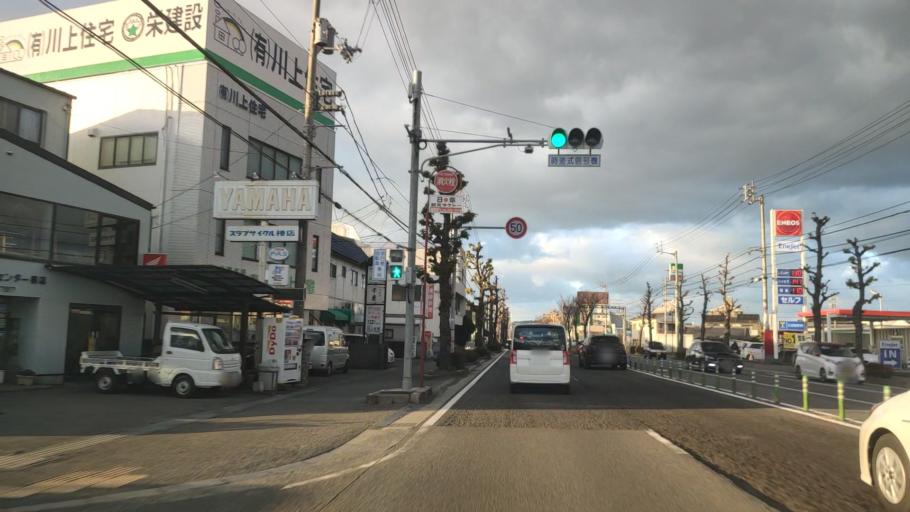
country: JP
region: Ehime
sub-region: Shikoku-chuo Shi
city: Matsuyama
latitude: 33.8068
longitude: 132.7812
